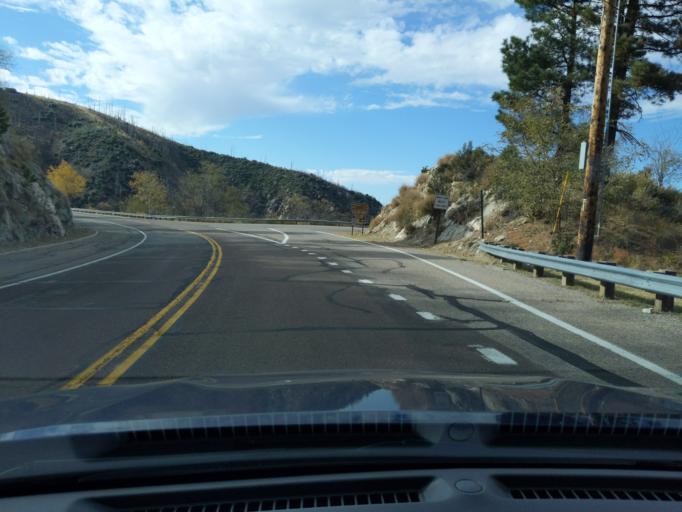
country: US
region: Arizona
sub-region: Pinal County
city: Oracle
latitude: 32.4480
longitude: -110.7544
